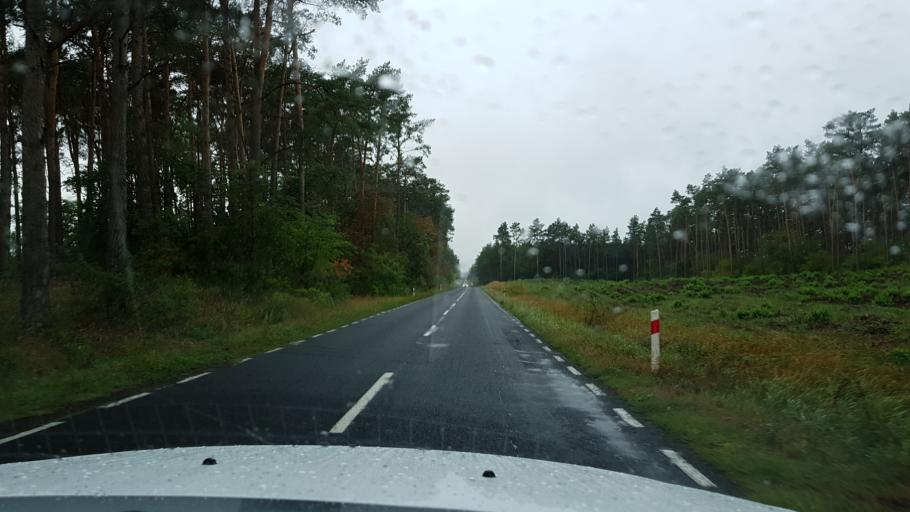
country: DE
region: Brandenburg
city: Schwedt (Oder)
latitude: 53.0437
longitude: 14.3354
